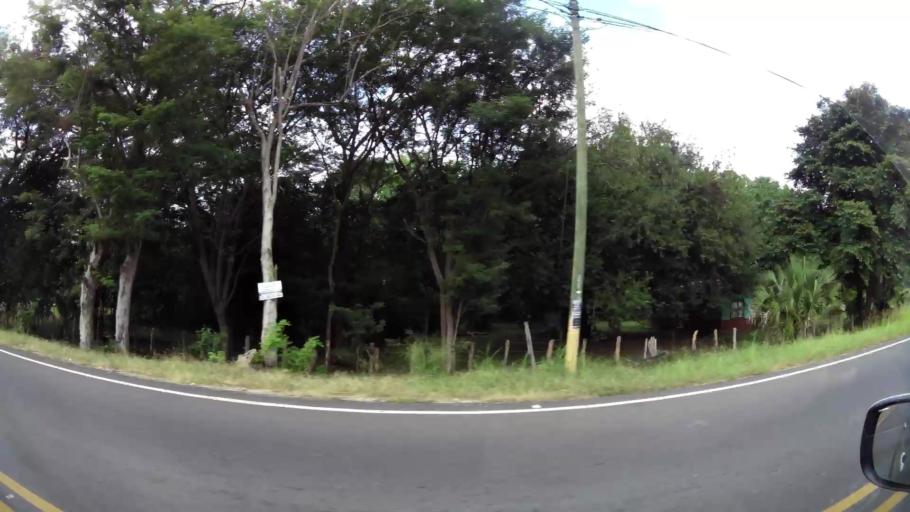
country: CR
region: Guanacaste
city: Hojancha
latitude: 10.1449
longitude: -85.3195
